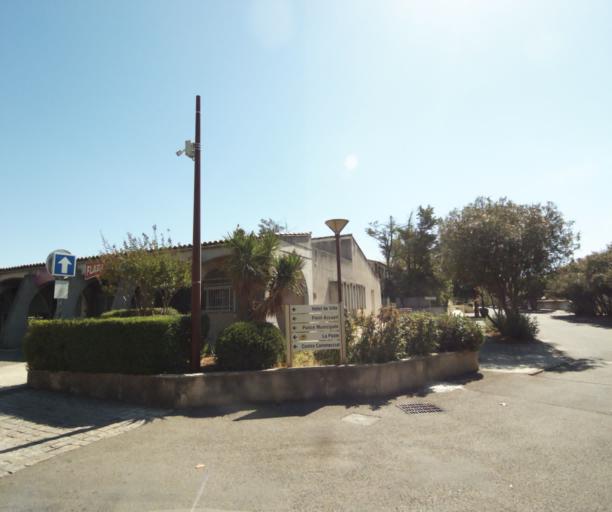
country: FR
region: Languedoc-Roussillon
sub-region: Departement du Gard
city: Rodilhan
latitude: 43.8260
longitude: 4.4307
